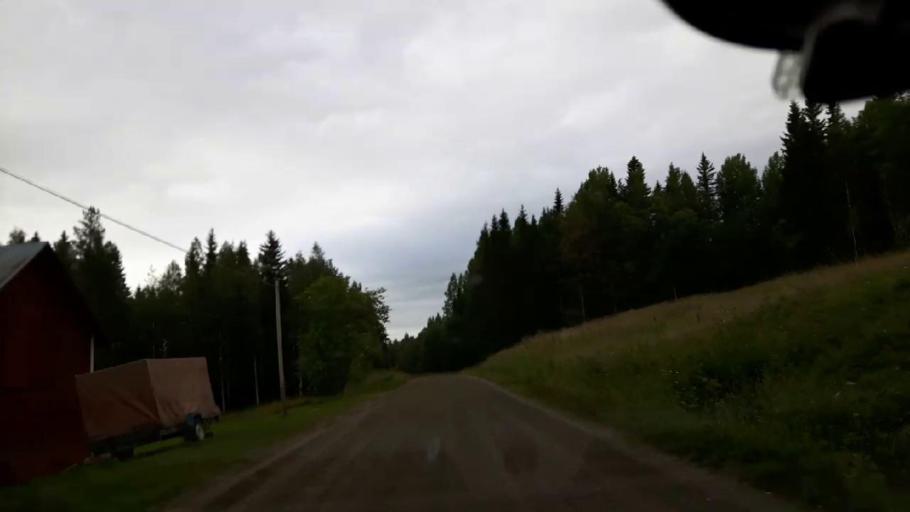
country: SE
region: Jaemtland
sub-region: Braecke Kommun
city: Braecke
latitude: 62.9065
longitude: 15.5925
